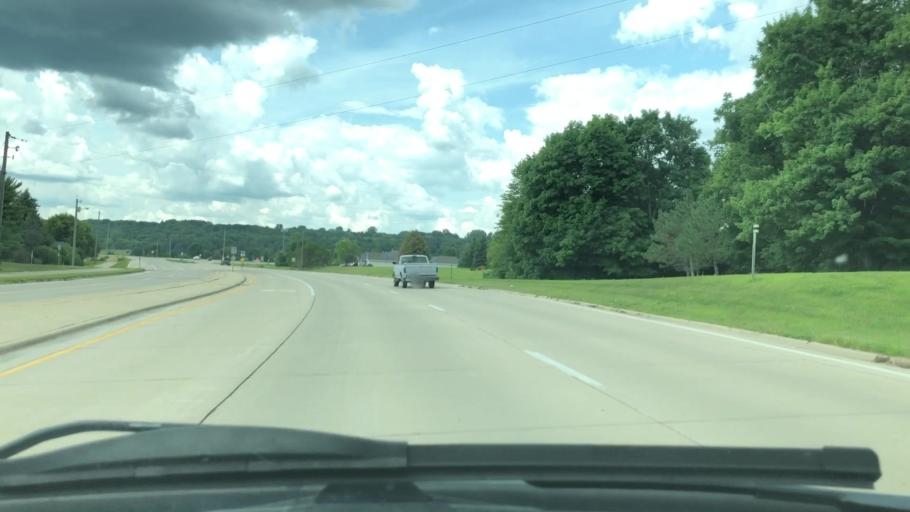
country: US
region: Minnesota
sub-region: Olmsted County
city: Rochester
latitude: 44.0021
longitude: -92.5029
